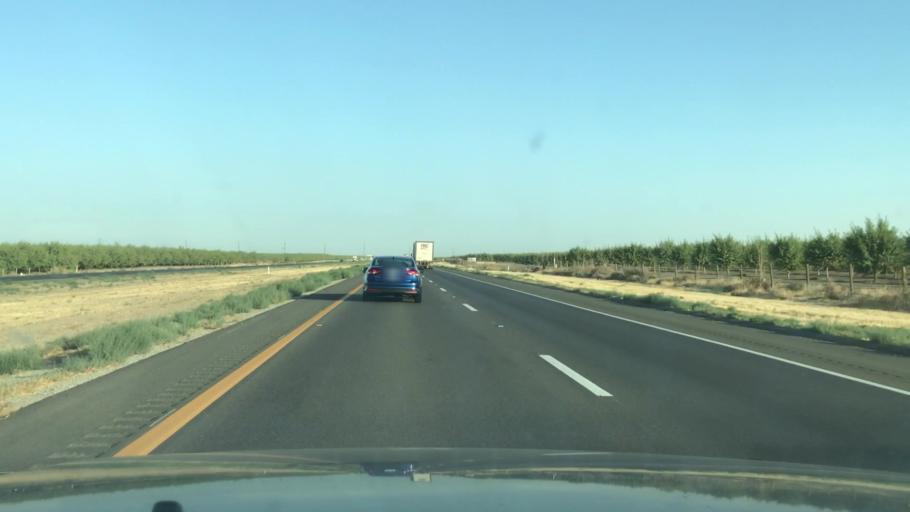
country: US
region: California
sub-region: Kings County
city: Kettleman City
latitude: 35.9559
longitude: -119.9341
